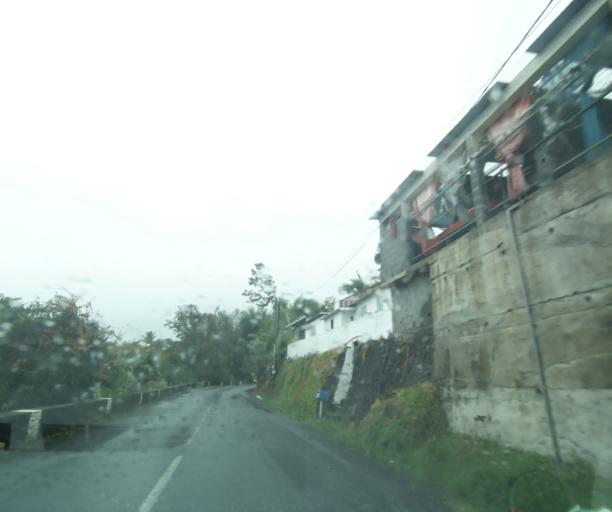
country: RE
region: Reunion
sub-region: Reunion
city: Saint-Paul
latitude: -21.0203
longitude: 55.3003
